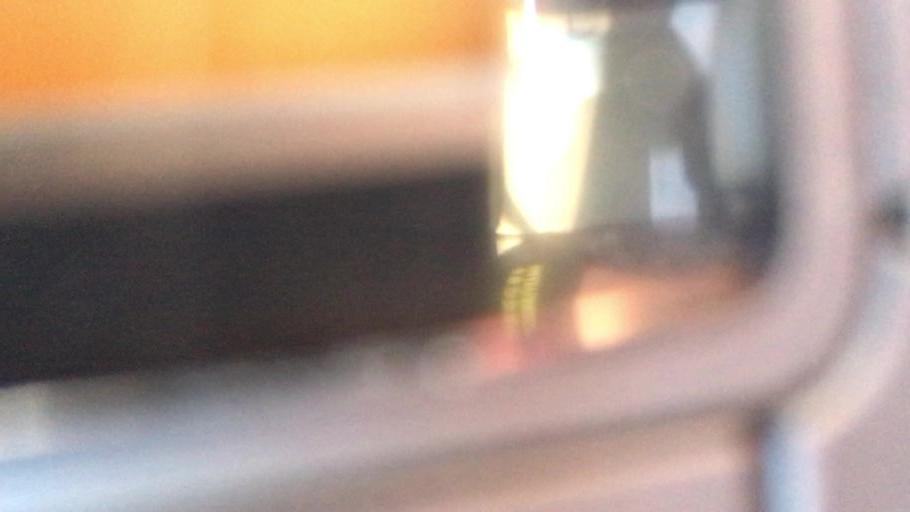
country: US
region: Maryland
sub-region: Wicomico County
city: Fruitland
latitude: 38.3281
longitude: -75.6239
